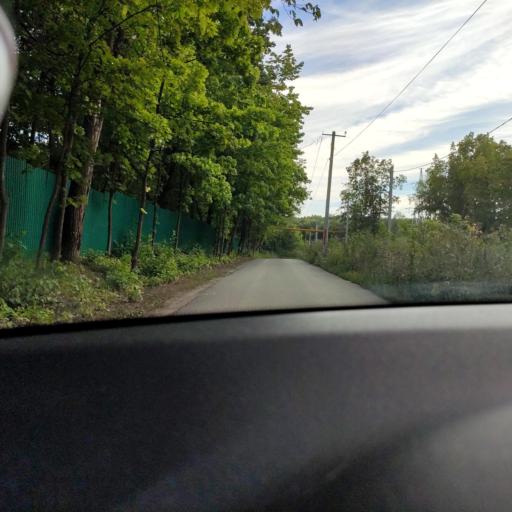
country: RU
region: Samara
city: Novosemeykino
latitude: 53.3475
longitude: 50.2443
